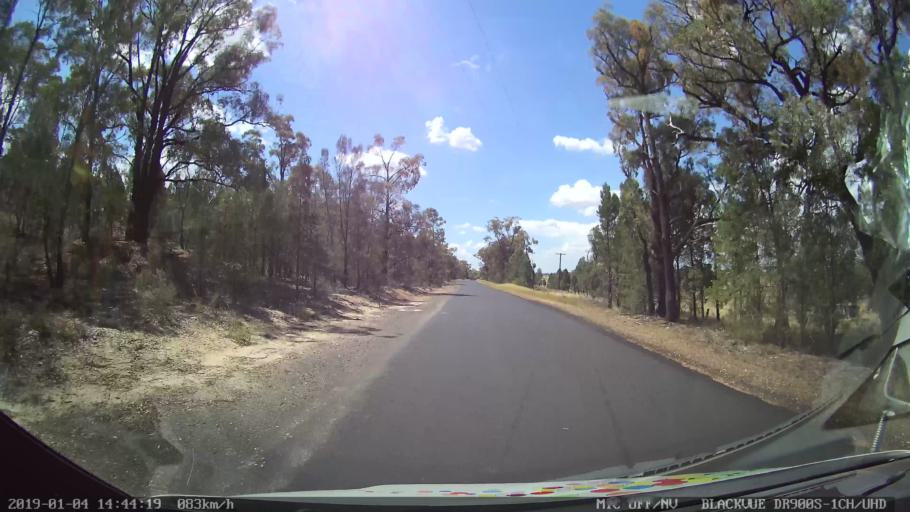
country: AU
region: New South Wales
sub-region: Dubbo Municipality
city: Dubbo
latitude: -32.1077
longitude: 148.6554
